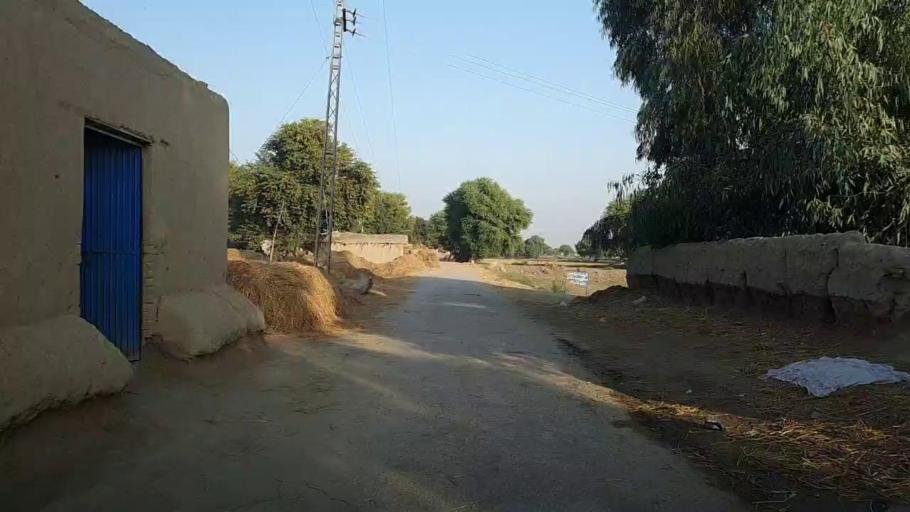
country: PK
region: Sindh
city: Kashmor
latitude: 28.4283
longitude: 69.4660
